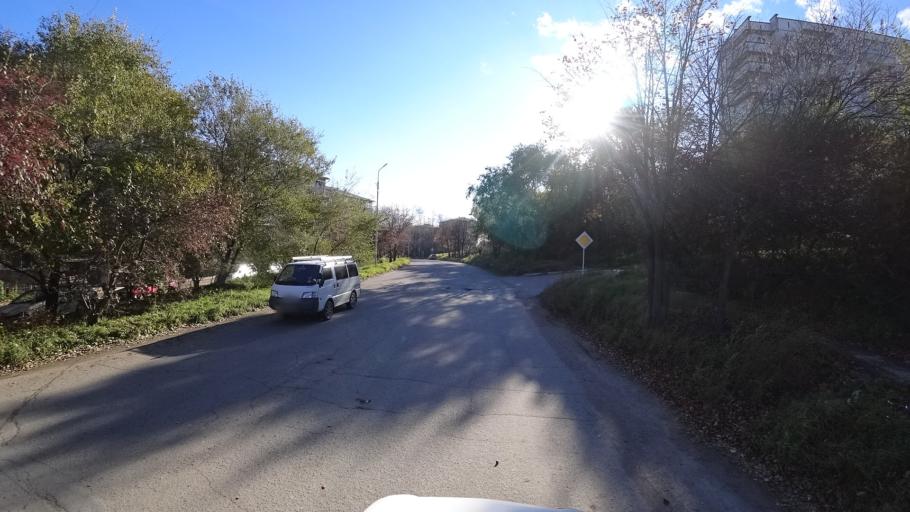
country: RU
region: Khabarovsk Krai
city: Amursk
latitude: 50.2417
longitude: 136.9054
